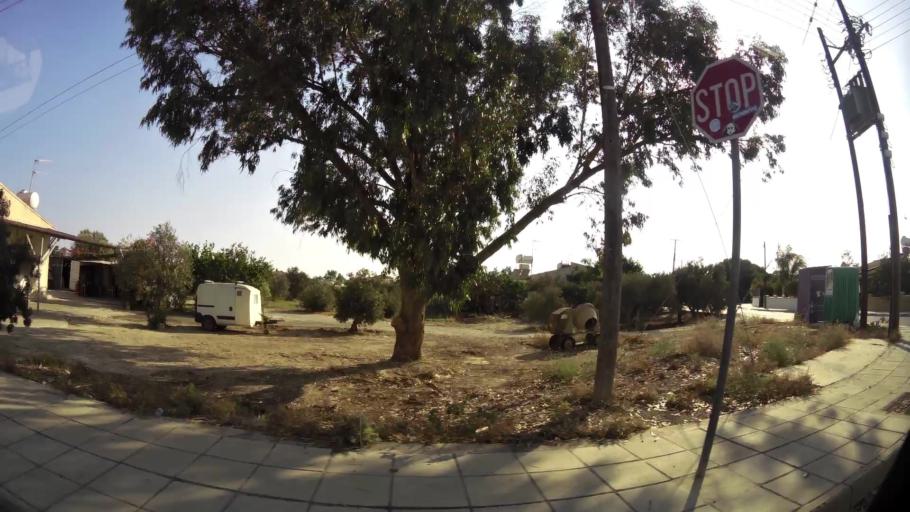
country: CY
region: Larnaka
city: Dhromolaxia
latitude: 34.8739
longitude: 33.5914
